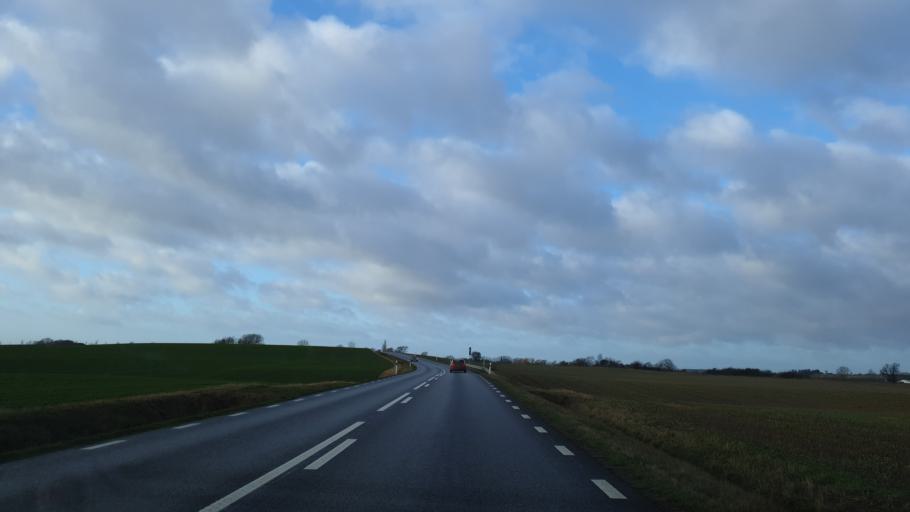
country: SE
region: Skane
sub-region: Trelleborgs Kommun
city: Trelleborg
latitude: 55.4582
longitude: 13.1642
